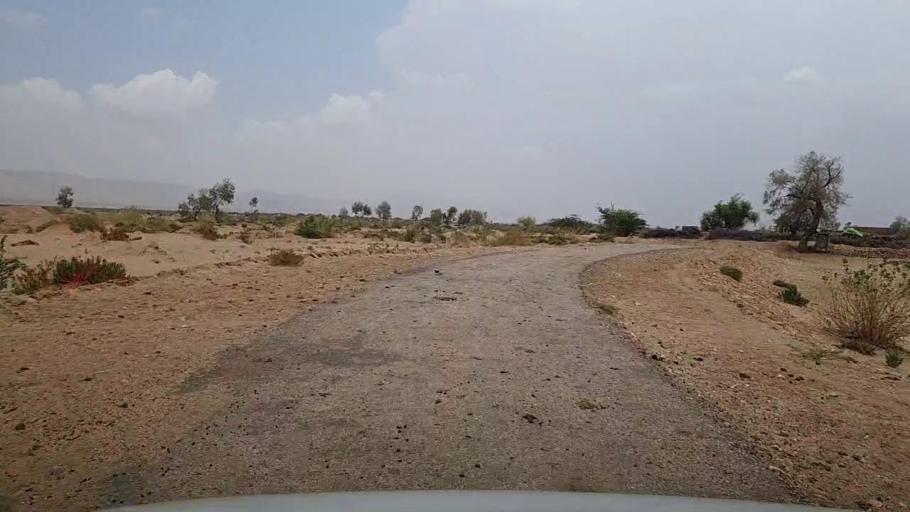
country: PK
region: Sindh
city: Sehwan
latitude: 26.3464
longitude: 67.7950
